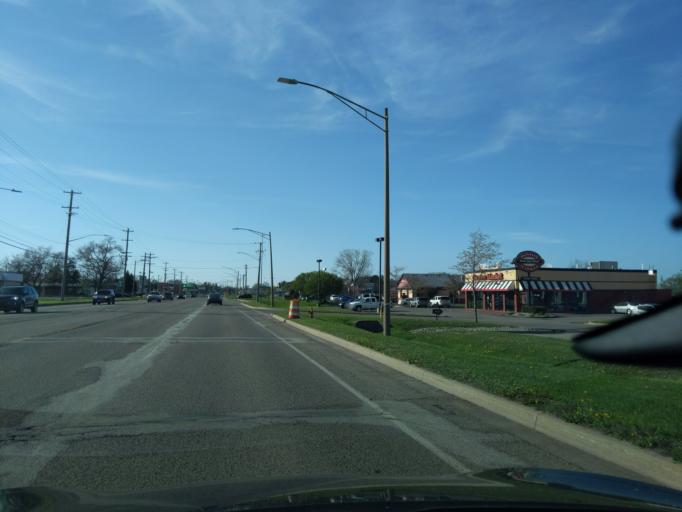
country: US
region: Michigan
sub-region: Ingham County
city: Holt
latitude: 42.6636
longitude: -84.5401
